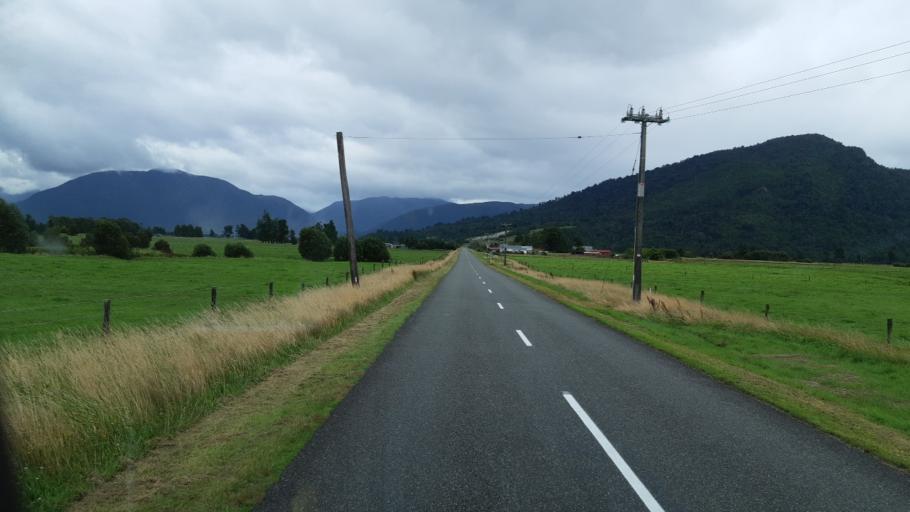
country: NZ
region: West Coast
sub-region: Westland District
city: Hokitika
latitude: -42.8713
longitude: 171.0178
